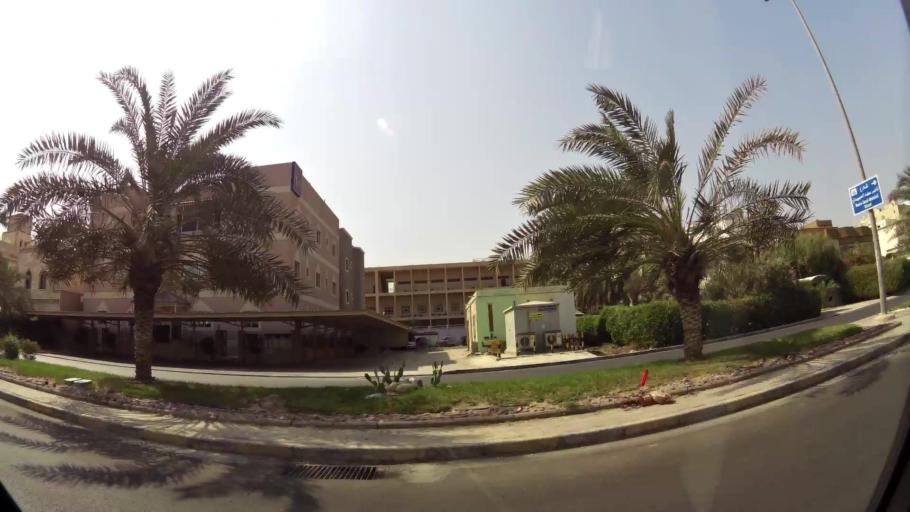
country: KW
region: Al Asimah
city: Ad Dasmah
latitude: 29.3502
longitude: 47.9985
